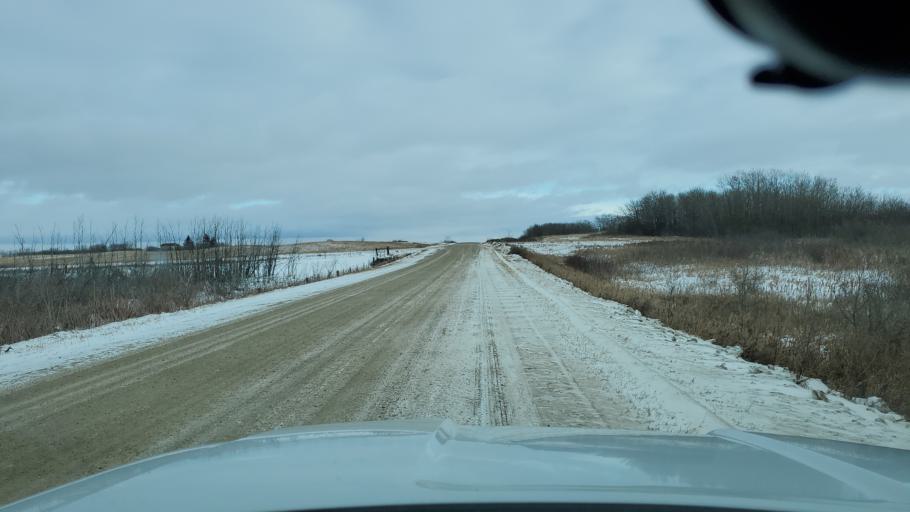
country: CA
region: Saskatchewan
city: White City
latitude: 50.7467
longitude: -104.1564
